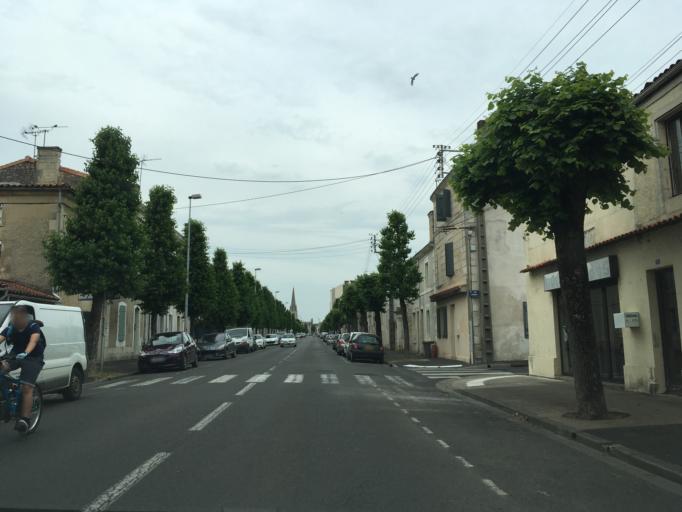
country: FR
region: Poitou-Charentes
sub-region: Departement des Deux-Sevres
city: Niort
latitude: 46.3145
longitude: -0.4656
